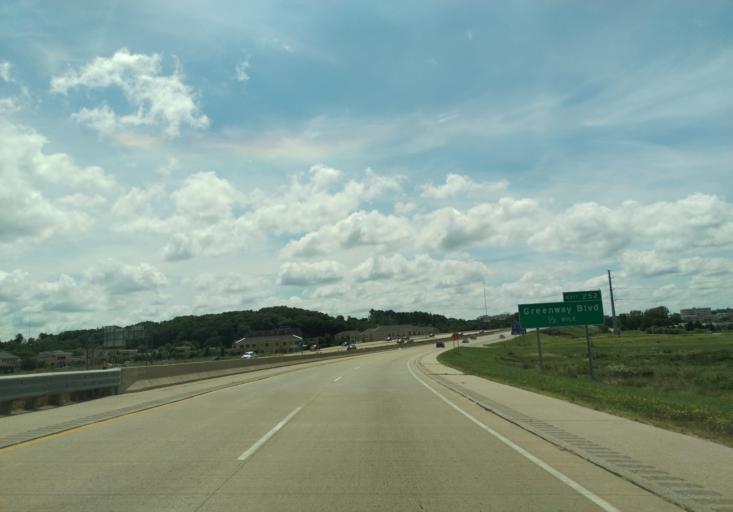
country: US
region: Wisconsin
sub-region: Dane County
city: Middleton
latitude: 43.0997
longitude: -89.5151
